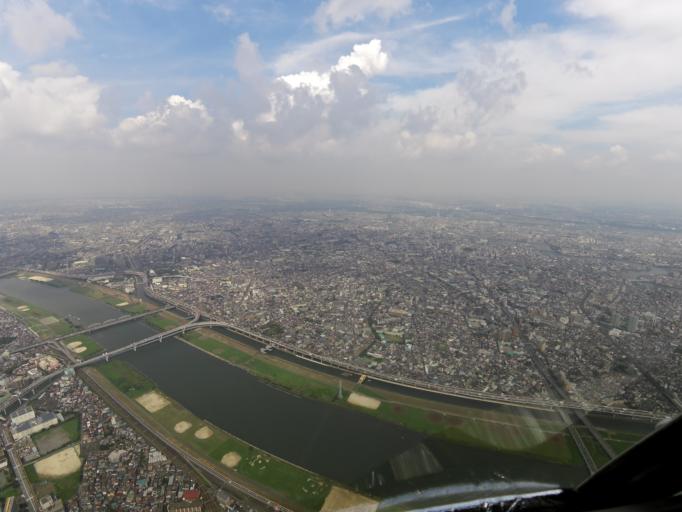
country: JP
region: Tokyo
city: Urayasu
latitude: 35.7304
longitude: 139.8204
